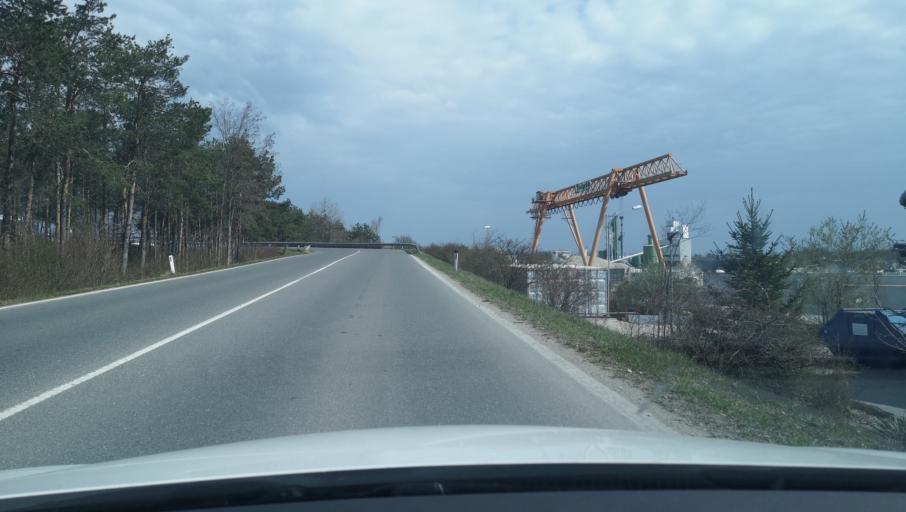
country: AT
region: Lower Austria
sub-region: Politischer Bezirk Amstetten
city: Winklarn
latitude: 48.1017
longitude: 14.8252
